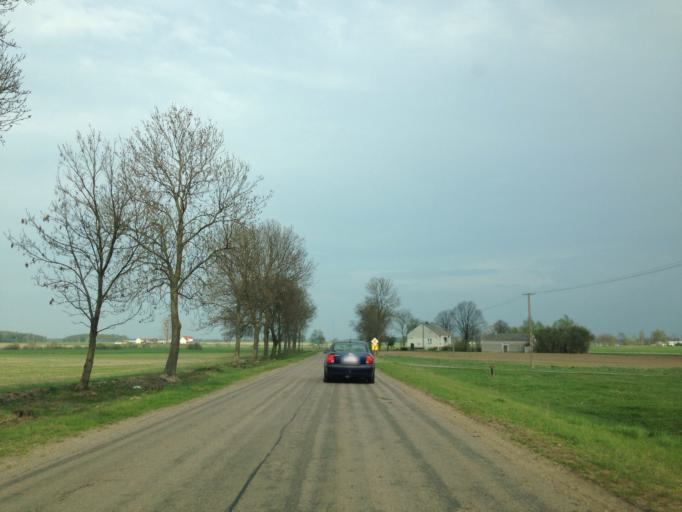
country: PL
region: Masovian Voivodeship
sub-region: Powiat zurominski
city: Siemiatkowo
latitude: 52.9763
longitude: 19.9963
